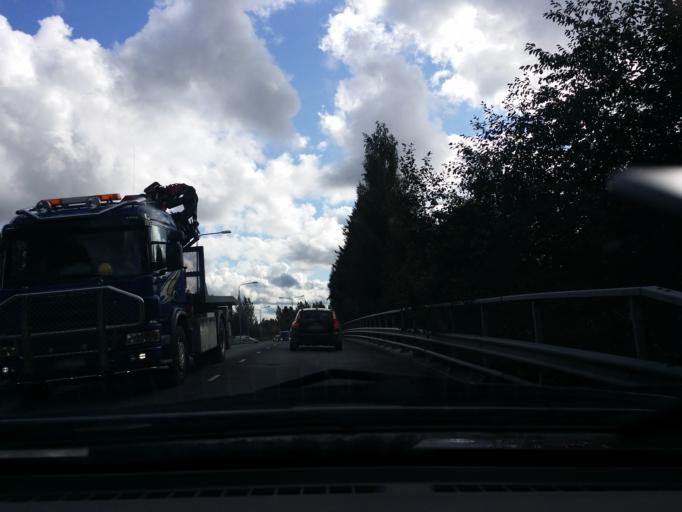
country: FI
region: Satakunta
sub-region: Pori
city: Pori
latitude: 61.4856
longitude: 21.8397
